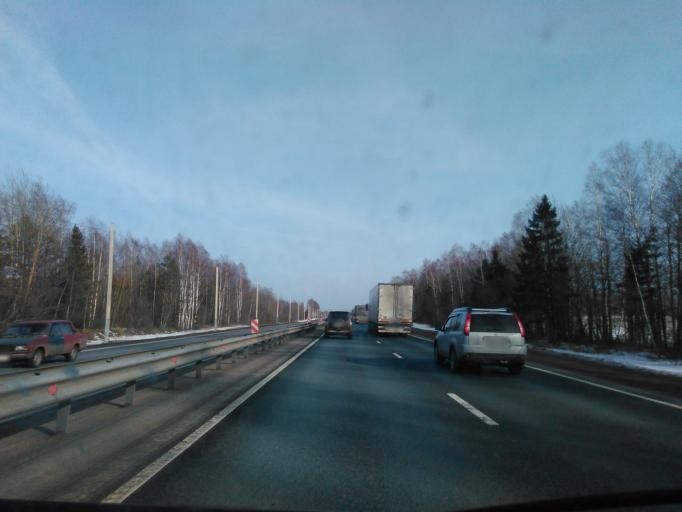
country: RU
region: Smolensk
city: Verkhnedneprovskiy
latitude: 55.1820
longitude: 33.5535
